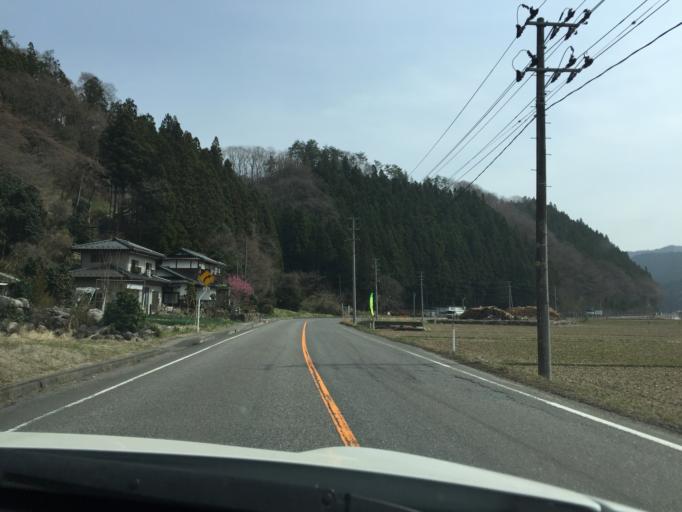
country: JP
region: Fukushima
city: Ishikawa
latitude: 37.0799
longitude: 140.5741
